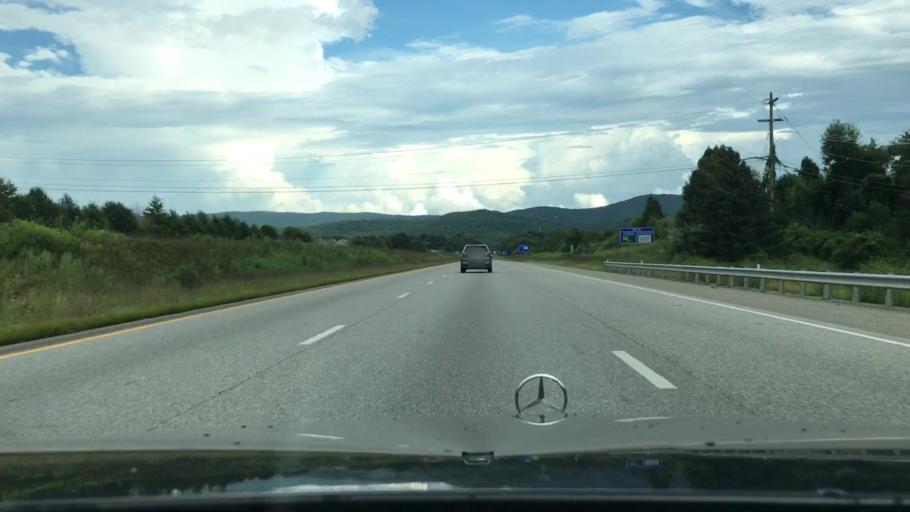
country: US
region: Virginia
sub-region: Augusta County
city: Lyndhurst
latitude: 38.0592
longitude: -78.9361
